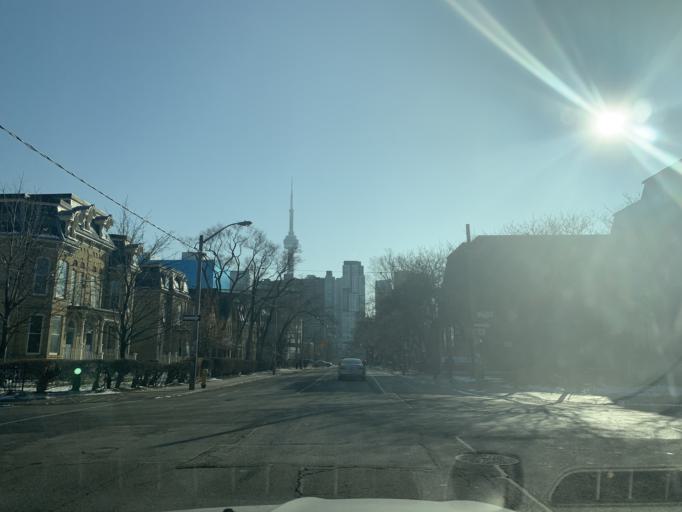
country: CA
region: Ontario
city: Toronto
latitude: 43.6550
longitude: -79.3943
